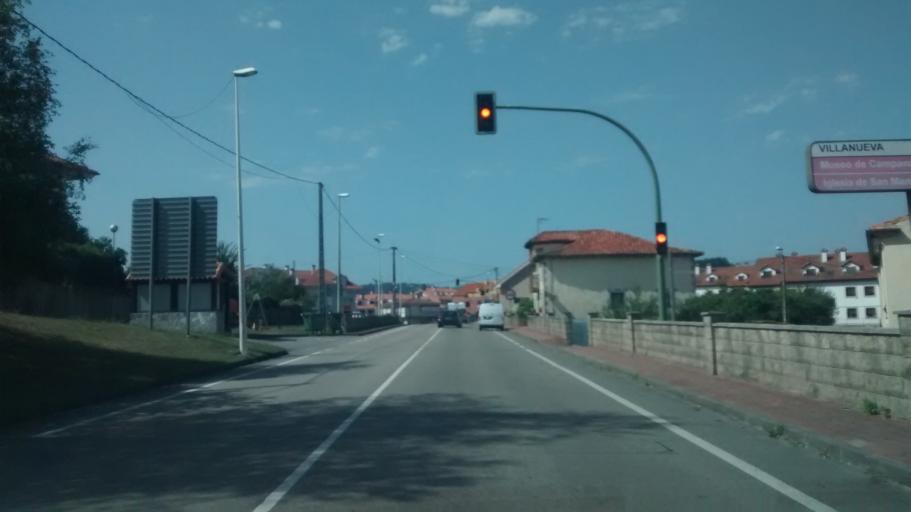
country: ES
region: Cantabria
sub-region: Provincia de Cantabria
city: San Miguel de Meruelo
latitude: 43.4467
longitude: -3.5638
